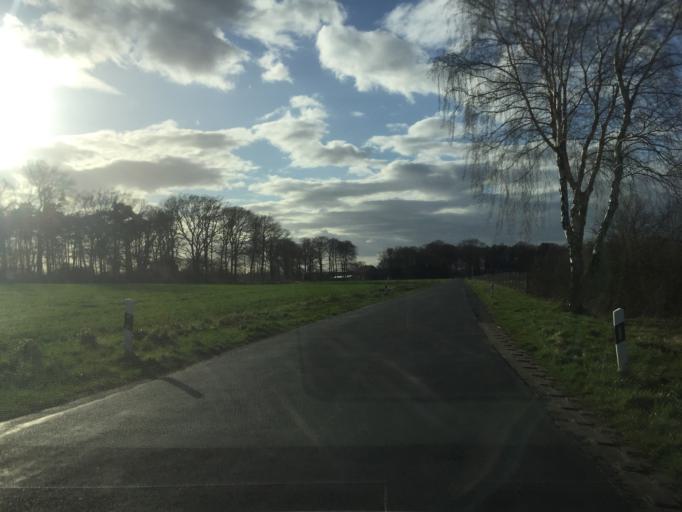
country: DE
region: Lower Saxony
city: Uchte
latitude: 52.5543
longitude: 8.9153
